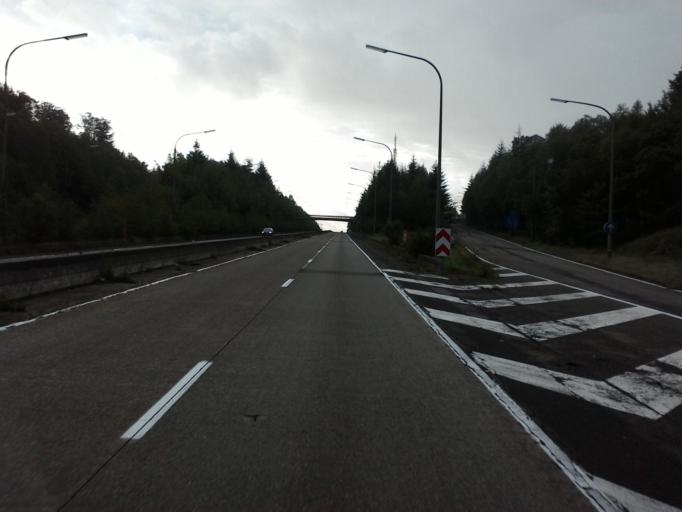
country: BE
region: Wallonia
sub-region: Province du Luxembourg
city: Martelange
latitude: 49.7849
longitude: 5.7479
